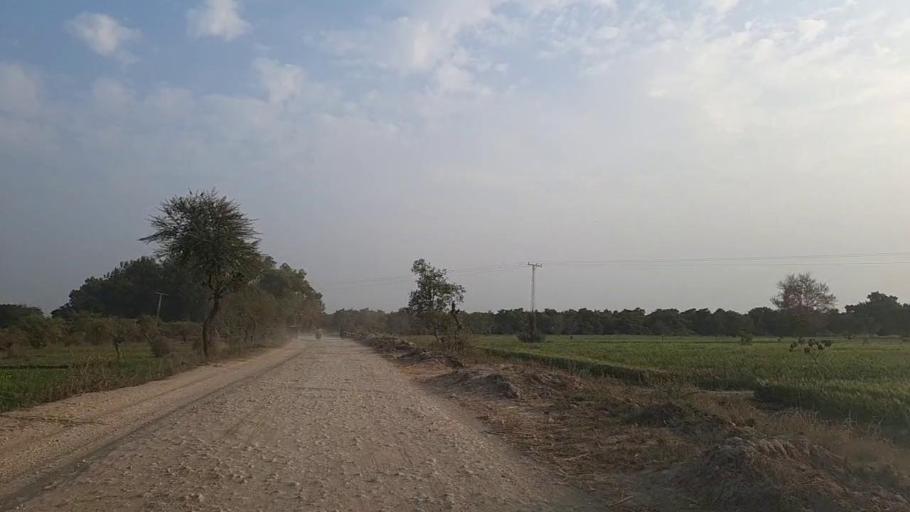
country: PK
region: Sindh
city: Mirwah Gorchani
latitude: 25.3079
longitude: 69.2118
